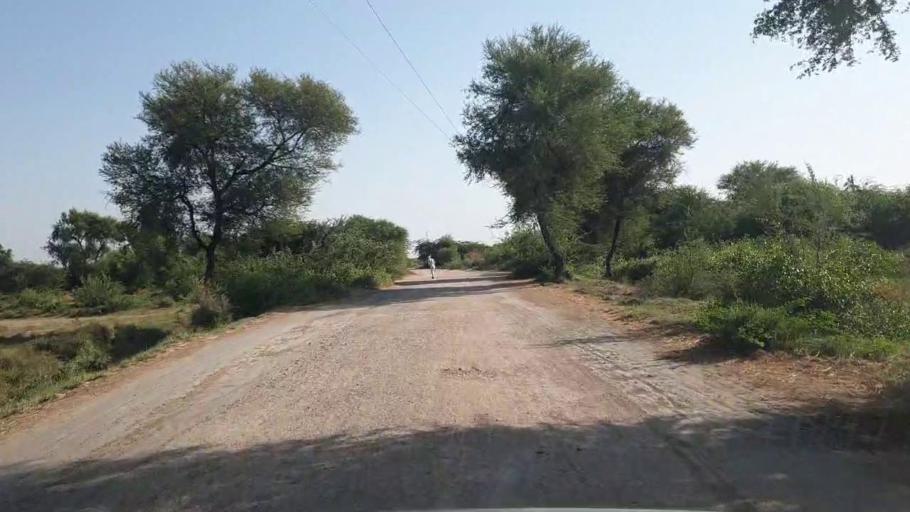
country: PK
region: Sindh
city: Matli
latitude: 25.0555
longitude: 68.7194
